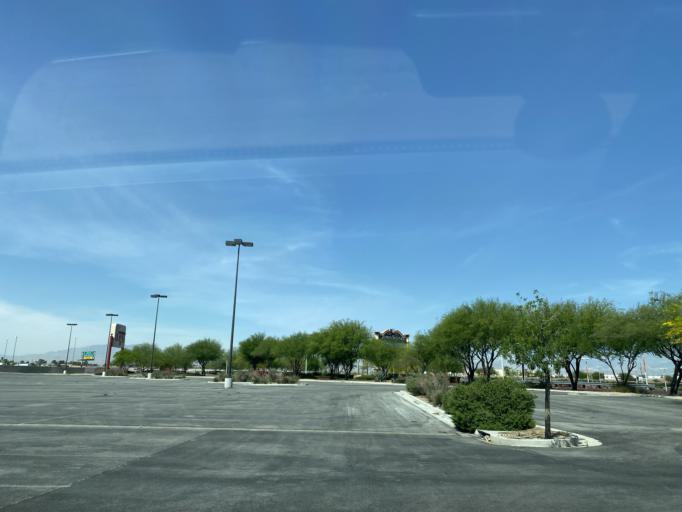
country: US
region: Nevada
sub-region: Clark County
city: Paradise
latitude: 36.0654
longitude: -115.1767
